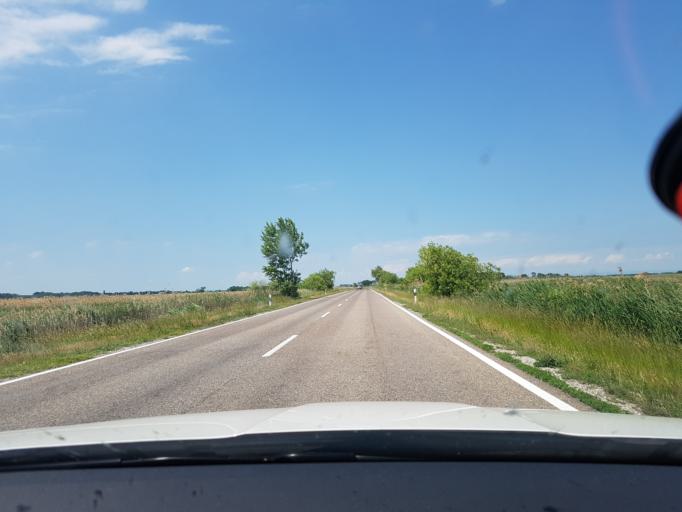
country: HU
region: Hajdu-Bihar
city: Egyek
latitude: 47.5561
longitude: 20.8709
